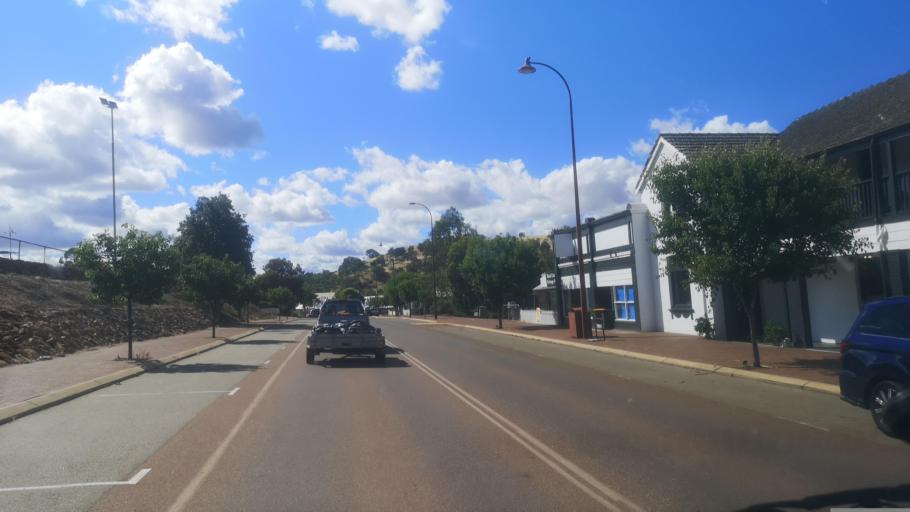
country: AU
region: Western Australia
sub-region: Toodyay
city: Toodyay
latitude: -31.5516
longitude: 116.4707
